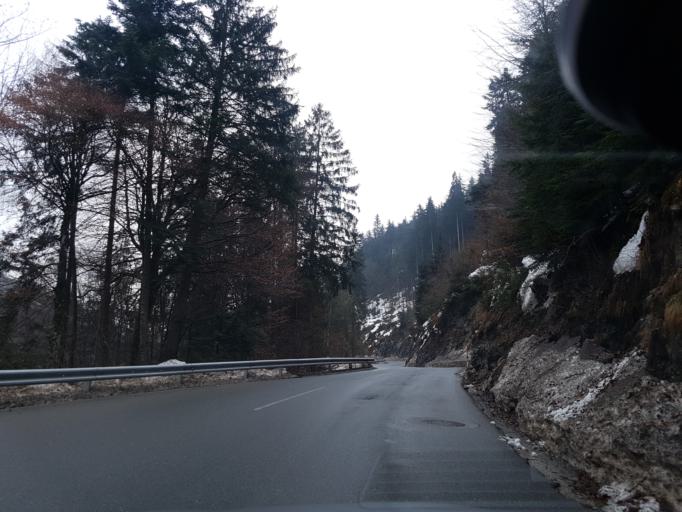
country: AT
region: Tyrol
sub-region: Politischer Bezirk Kufstein
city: Worgl
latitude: 47.4741
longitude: 12.0728
